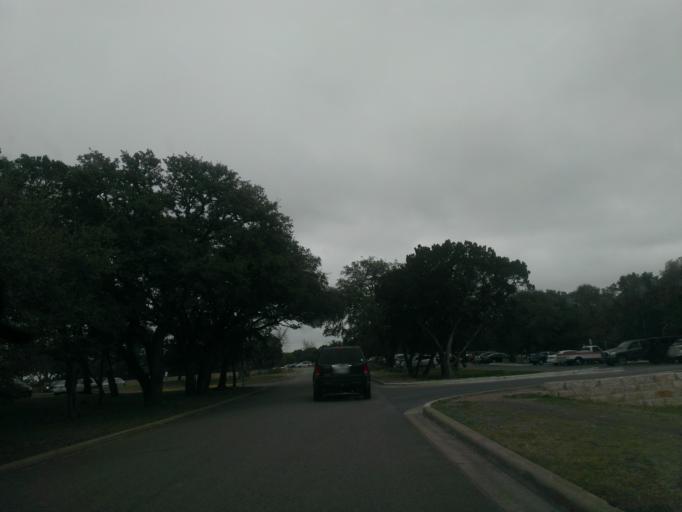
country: US
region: Texas
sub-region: Travis County
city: Wells Branch
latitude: 30.4019
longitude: -97.6849
